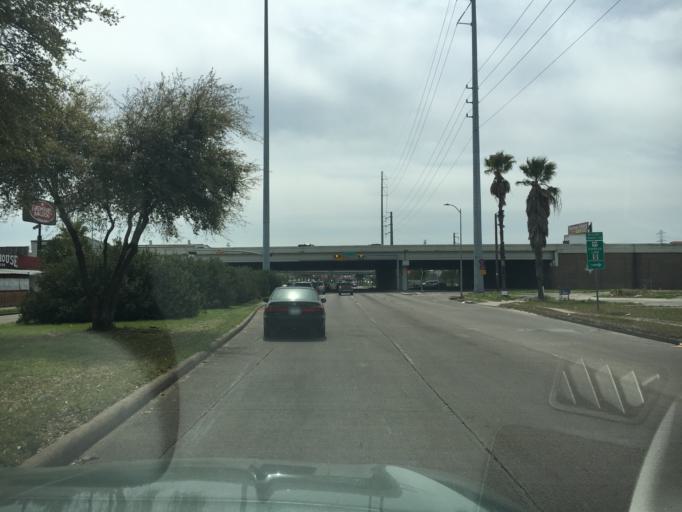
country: US
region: Texas
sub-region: Harris County
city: Bellaire
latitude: 29.7270
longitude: -95.4843
